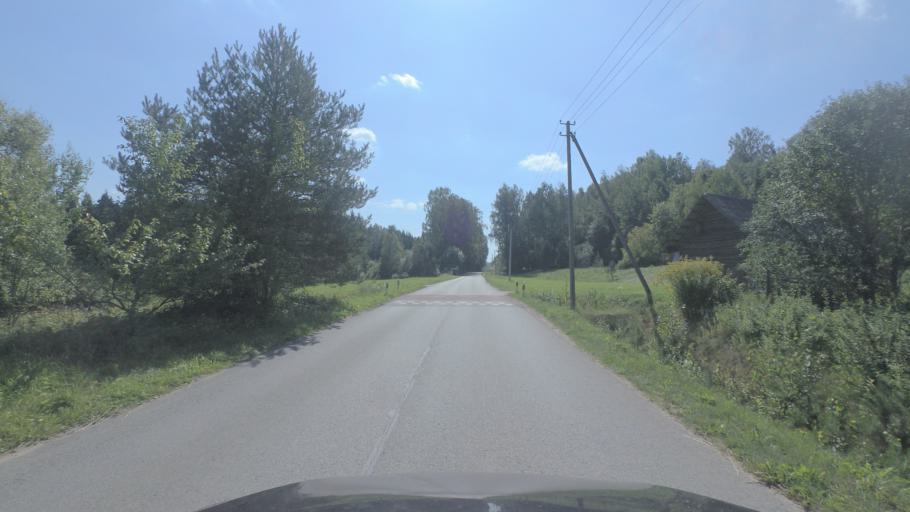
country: LT
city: Nemencine
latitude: 54.8455
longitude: 25.3729
